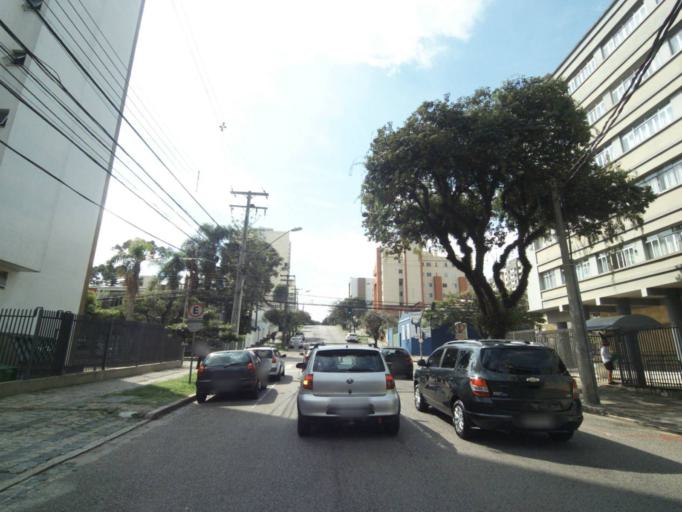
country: BR
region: Parana
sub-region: Curitiba
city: Curitiba
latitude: -25.4292
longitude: -49.2616
